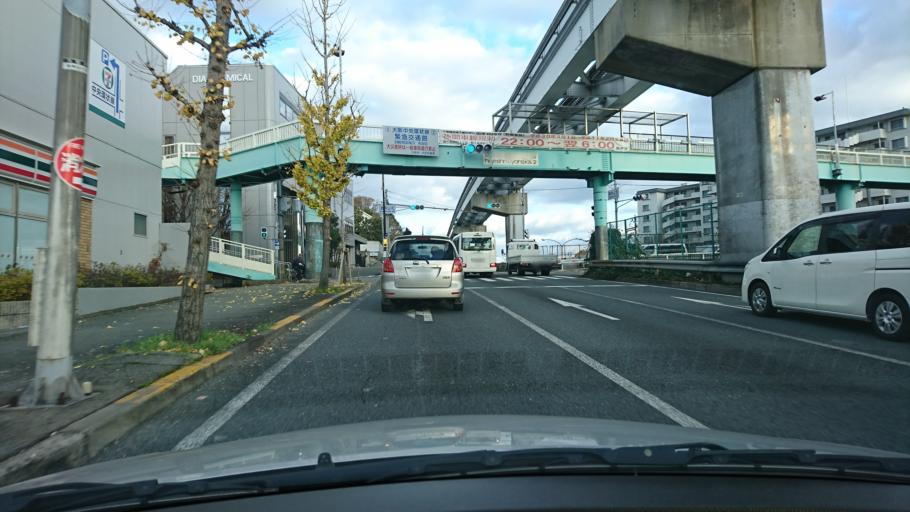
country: JP
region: Osaka
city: Mino
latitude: 34.8060
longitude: 135.4819
